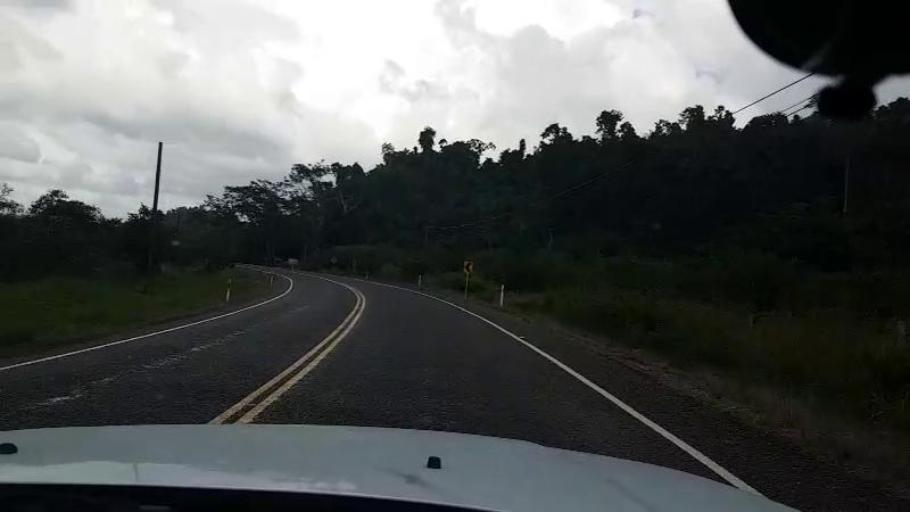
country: BZ
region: Cayo
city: Belmopan
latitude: 17.1470
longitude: -88.6961
